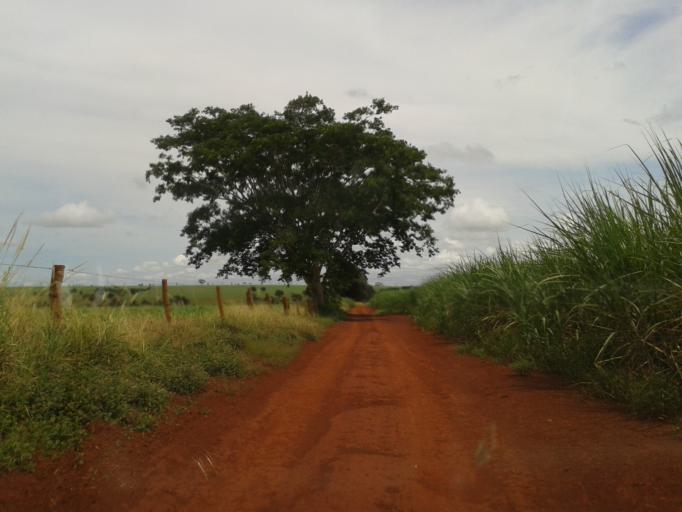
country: BR
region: Minas Gerais
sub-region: Centralina
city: Centralina
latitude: -18.6126
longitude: -49.2894
